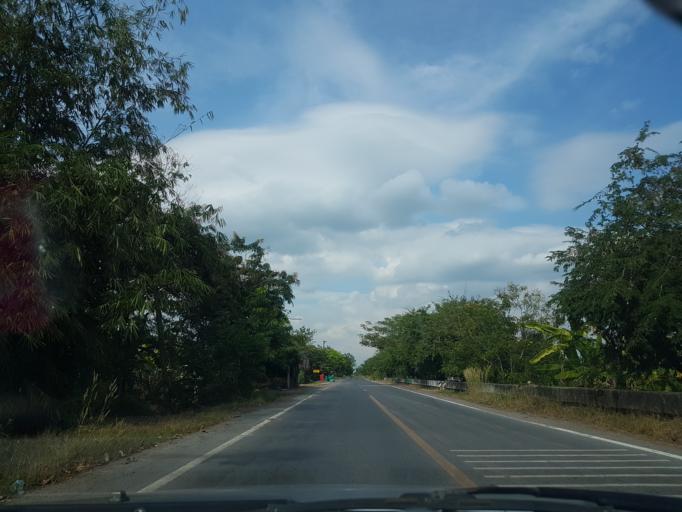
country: TH
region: Pathum Thani
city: Nong Suea
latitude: 14.1374
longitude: 100.8915
